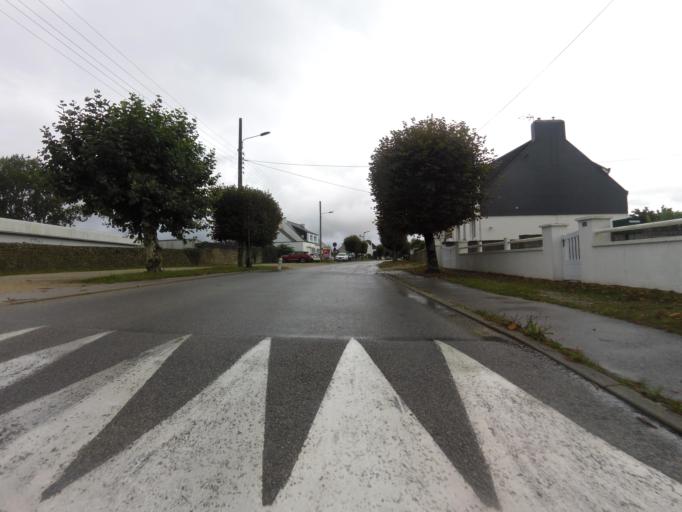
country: FR
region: Brittany
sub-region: Departement du Morbihan
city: Etel
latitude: 47.6611
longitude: -3.2013
